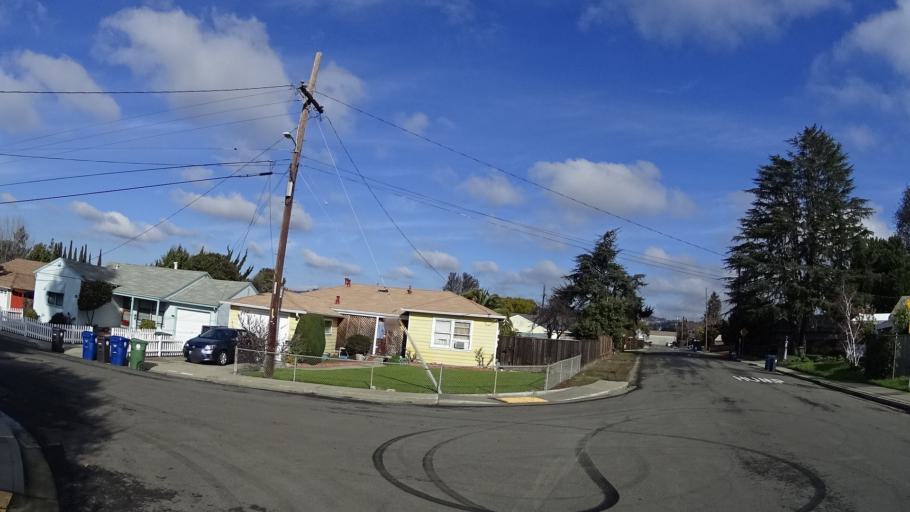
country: US
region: California
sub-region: Alameda County
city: Castro Valley
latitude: 37.6881
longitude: -122.0710
